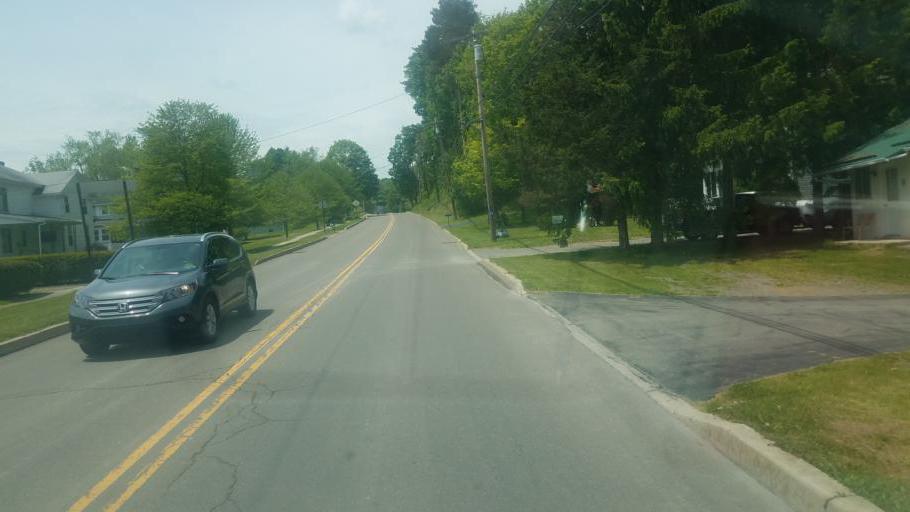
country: US
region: Pennsylvania
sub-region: Tioga County
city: Wellsboro
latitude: 41.7436
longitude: -77.3145
